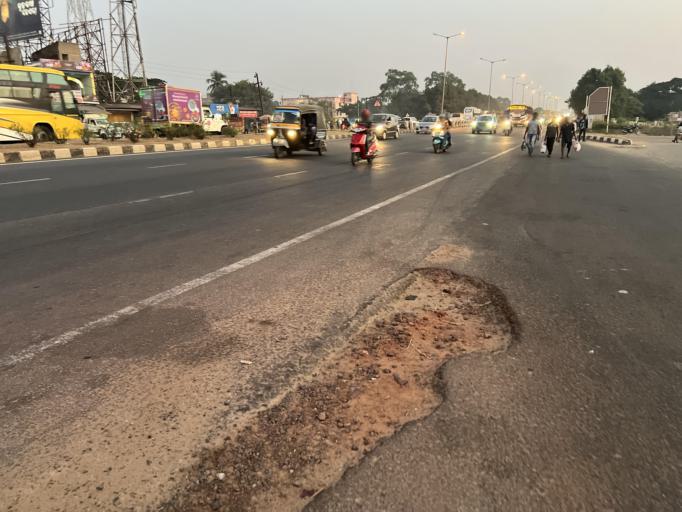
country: IN
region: Odisha
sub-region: Cuttack
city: Cuttack
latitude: 20.4031
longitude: 85.8804
